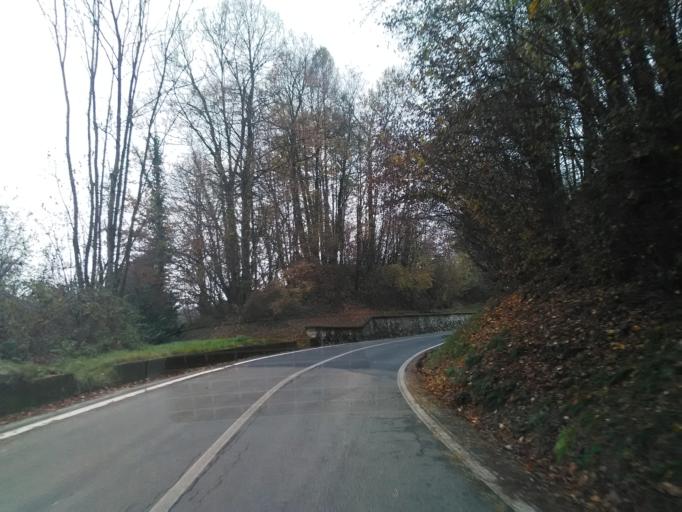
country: IT
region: Piedmont
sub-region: Provincia di Vercelli
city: Guardabosone
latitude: 45.6969
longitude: 8.2540
